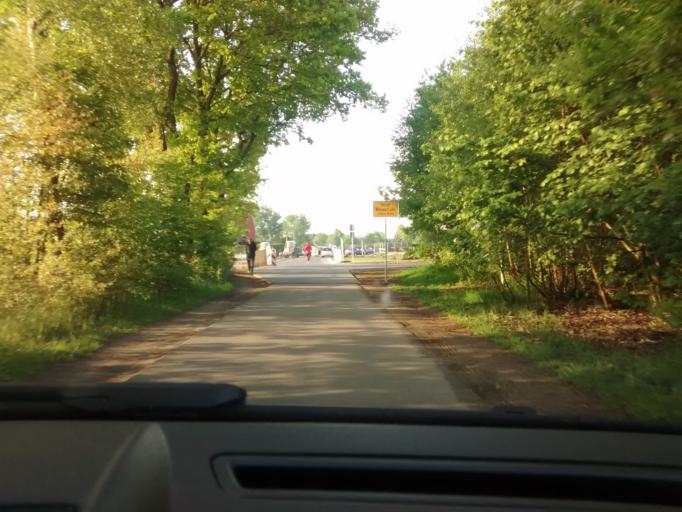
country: DE
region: Lower Saxony
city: Winsen
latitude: 53.3687
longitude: 10.1861
